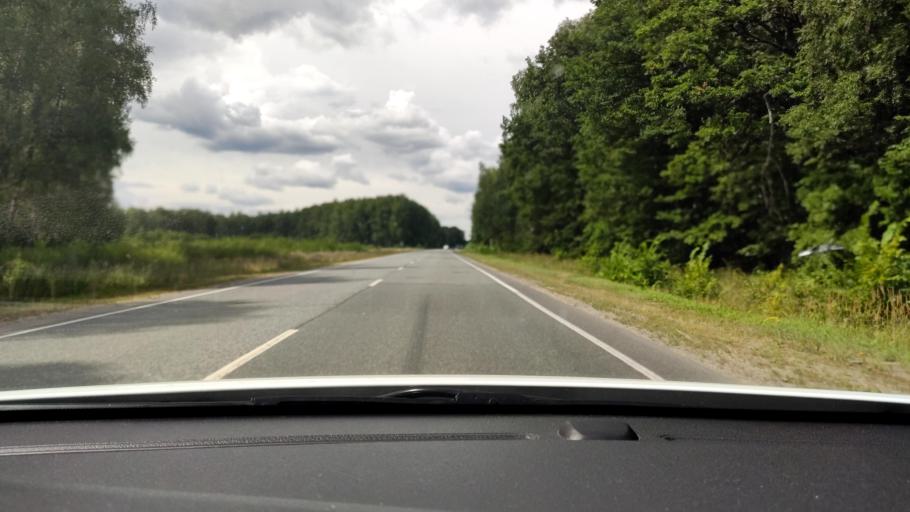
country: RU
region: Tatarstan
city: Aysha
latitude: 55.8864
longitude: 48.6058
